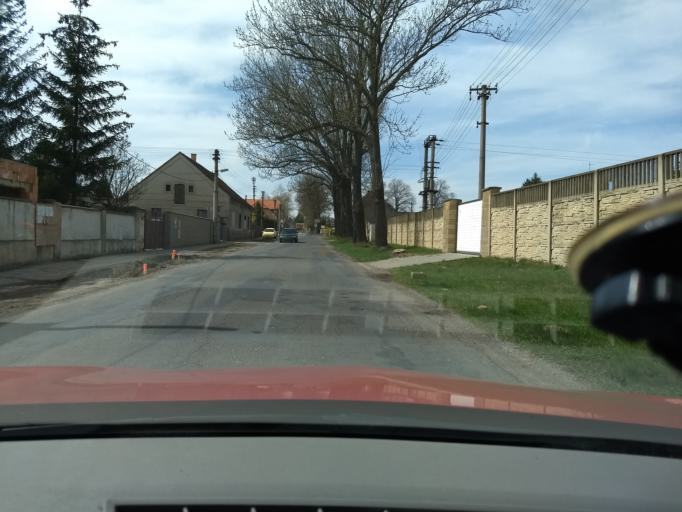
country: CZ
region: Central Bohemia
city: Rudna
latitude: 50.0459
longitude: 14.1844
